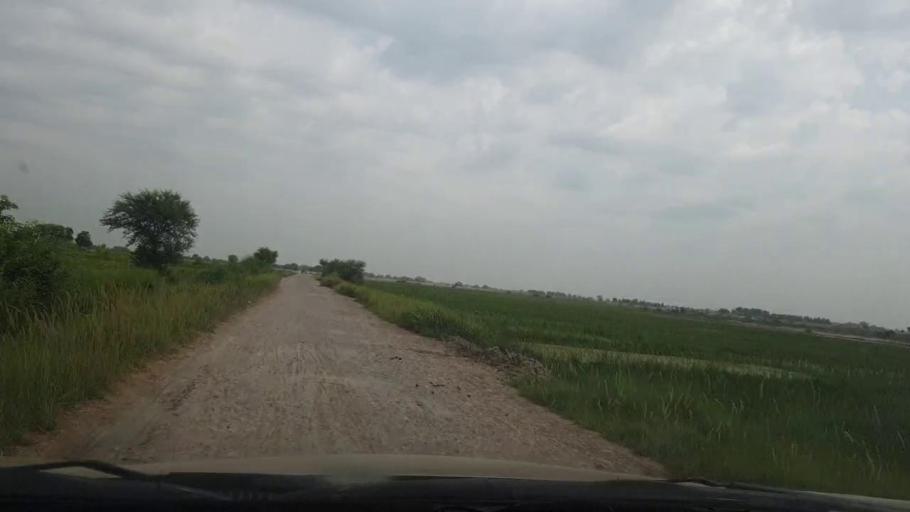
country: PK
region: Sindh
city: Ratodero
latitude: 27.7198
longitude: 68.2313
